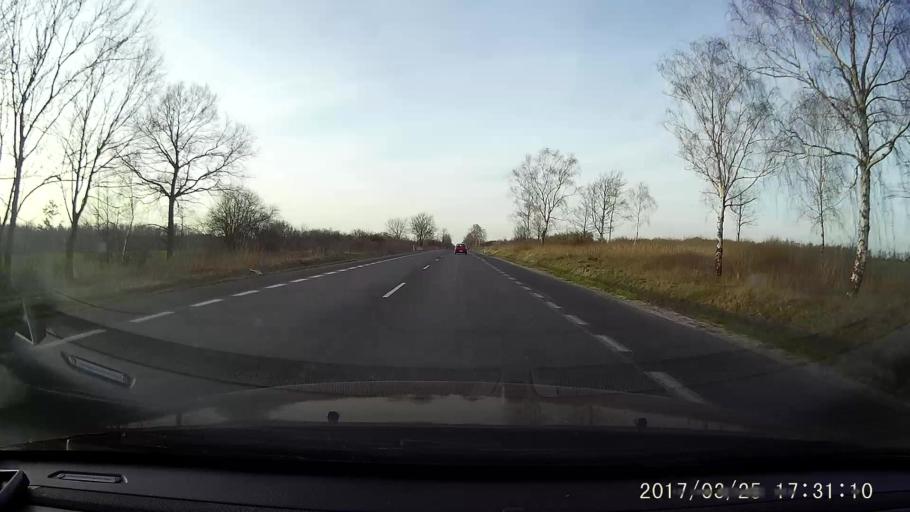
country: PL
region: Lower Silesian Voivodeship
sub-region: Powiat zgorzelecki
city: Zgorzelec
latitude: 51.0995
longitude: 15.0201
